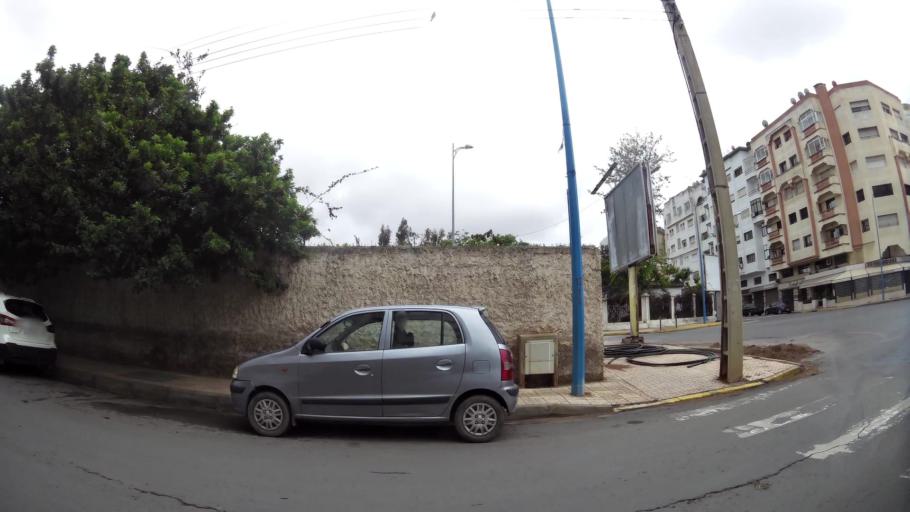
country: MA
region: Grand Casablanca
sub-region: Casablanca
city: Casablanca
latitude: 33.5754
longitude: -7.6123
